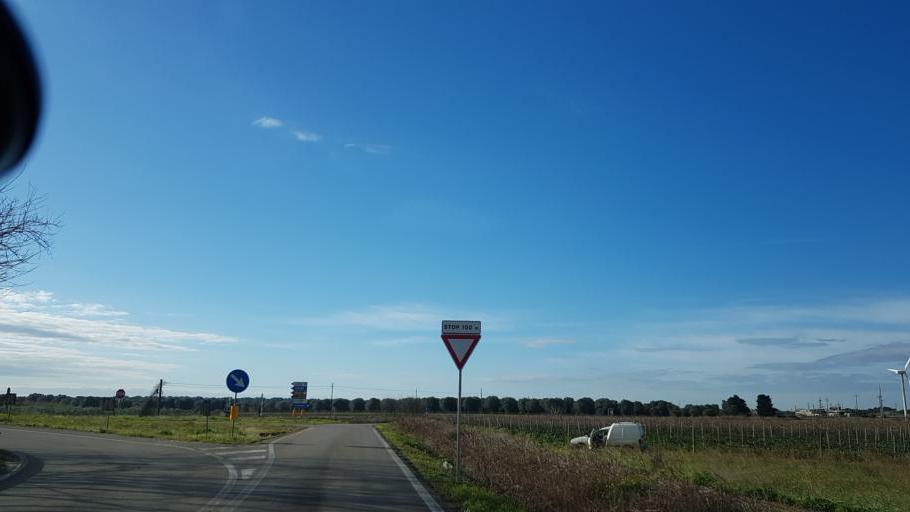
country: IT
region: Apulia
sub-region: Provincia di Brindisi
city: Tuturano
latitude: 40.5541
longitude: 17.9926
